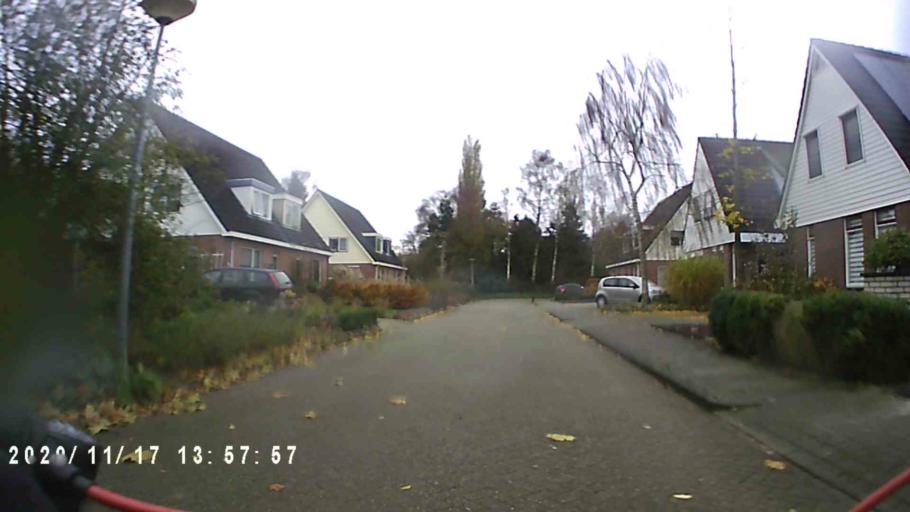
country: NL
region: Groningen
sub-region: Gemeente Zuidhorn
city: Grijpskerk
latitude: 53.2240
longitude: 6.3494
